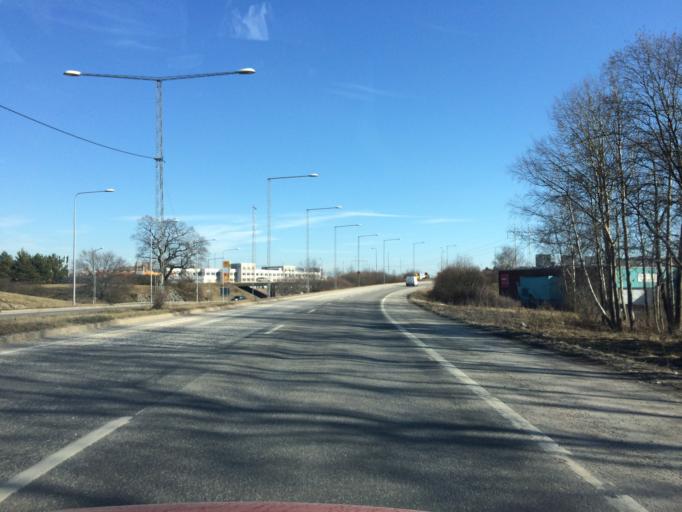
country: SE
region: Stockholm
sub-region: Huddinge Kommun
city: Segeltorp
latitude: 59.2884
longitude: 17.9440
